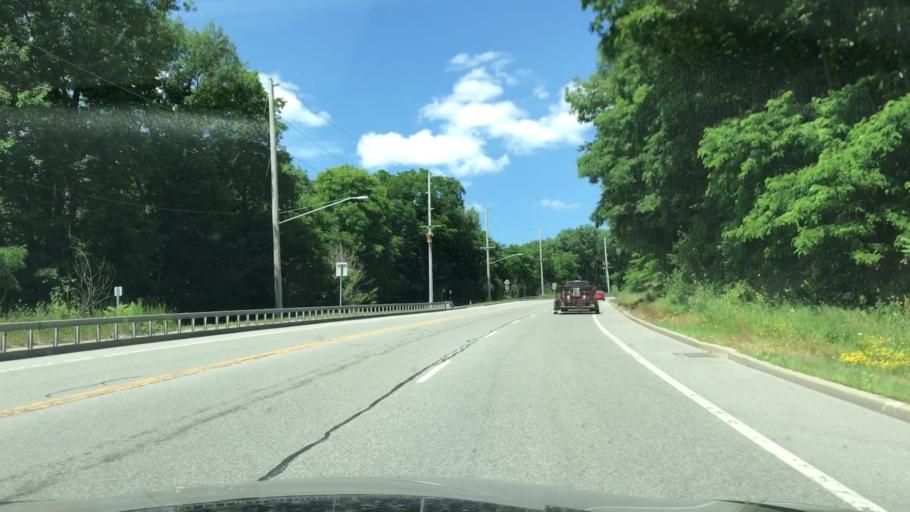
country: US
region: New York
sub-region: Wyoming County
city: Warsaw
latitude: 42.7437
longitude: -78.1274
